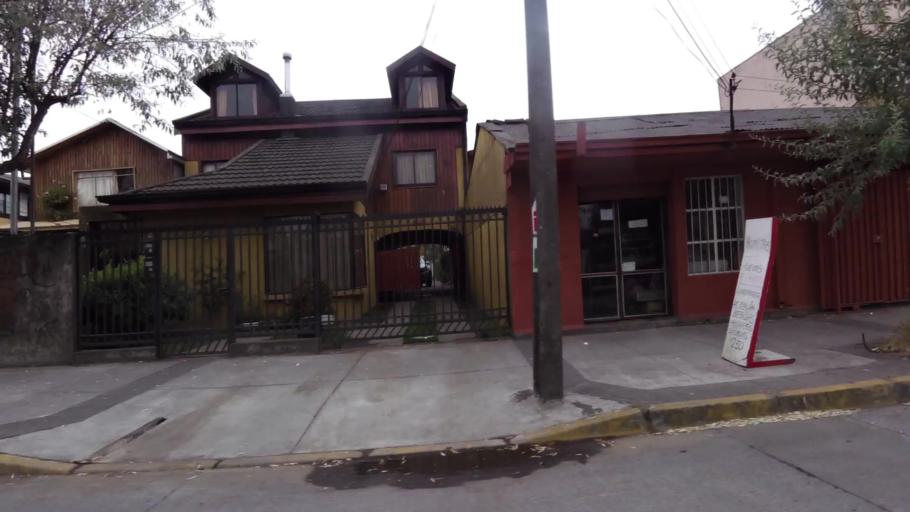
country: CL
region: Biobio
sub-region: Provincia de Concepcion
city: Concepcion
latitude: -36.8177
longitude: -73.0354
